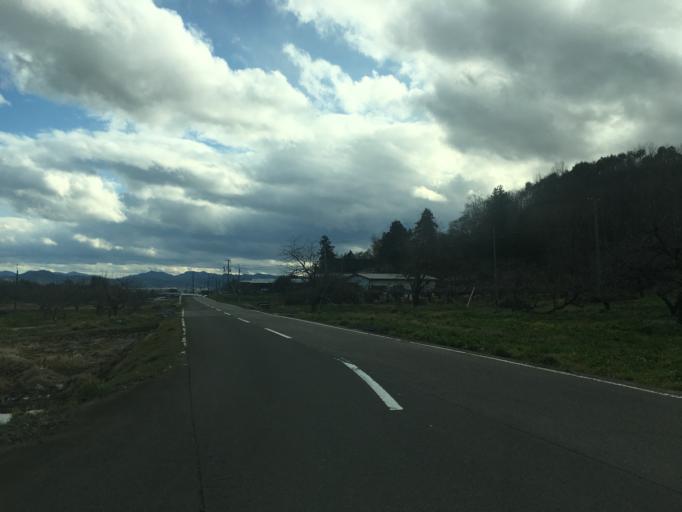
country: JP
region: Fukushima
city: Yanagawamachi-saiwaicho
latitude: 37.8857
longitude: 140.6007
